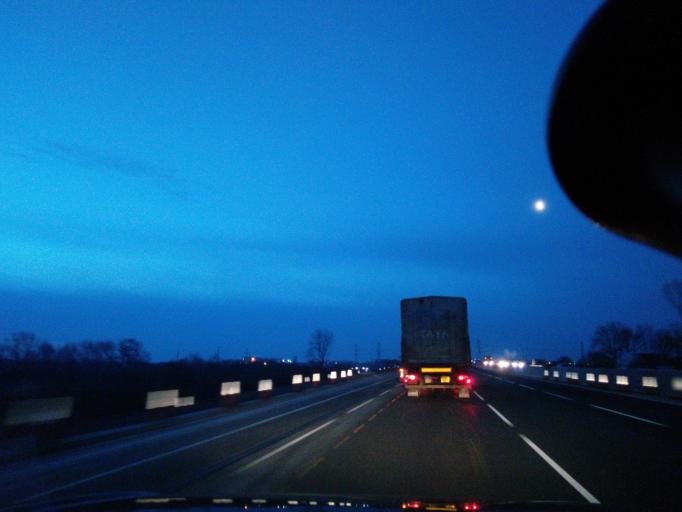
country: GB
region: England
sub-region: Leicestershire
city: Kegworth
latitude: 52.8635
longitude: -1.3038
